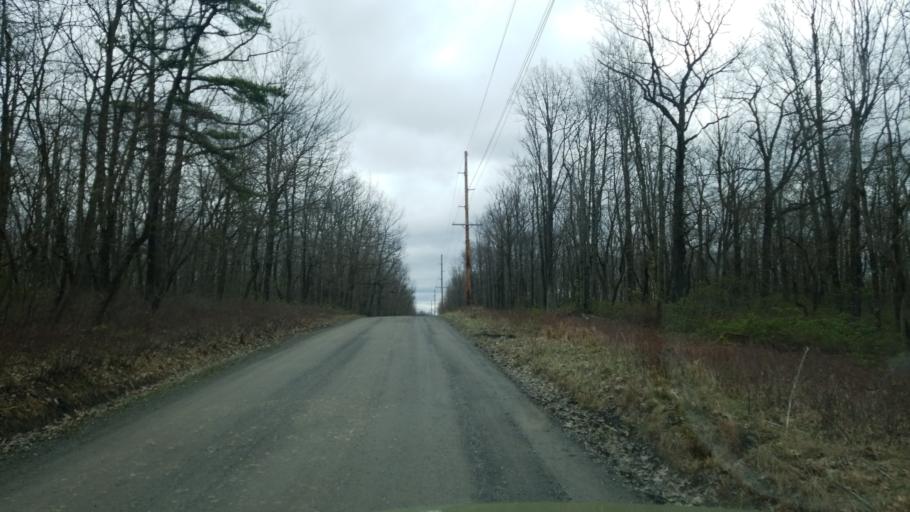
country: US
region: Pennsylvania
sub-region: Clearfield County
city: Shiloh
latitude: 41.1736
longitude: -78.3027
